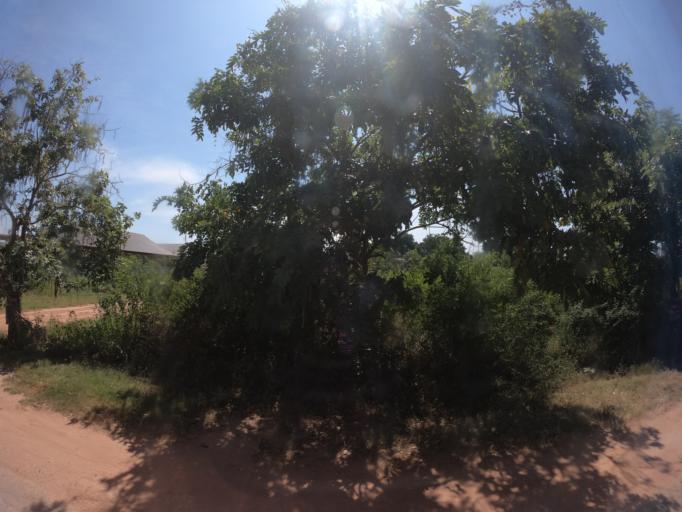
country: TH
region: Khon Kaen
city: Ban Phai
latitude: 16.0627
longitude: 102.7247
